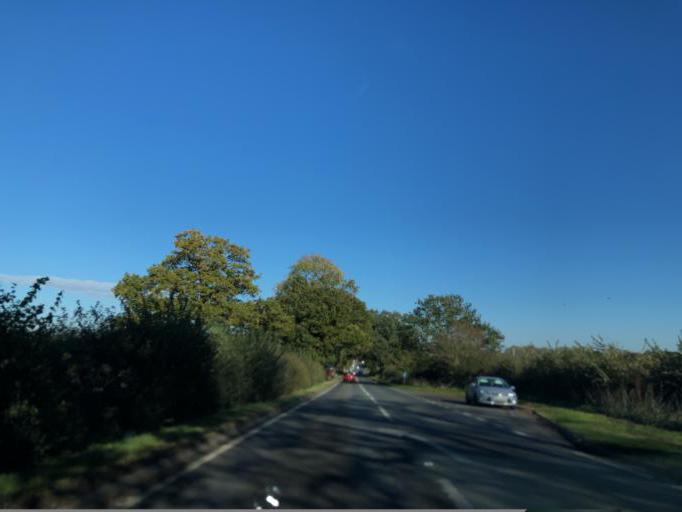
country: GB
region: England
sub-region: Warwickshire
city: Harbury
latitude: 52.2443
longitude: -1.4935
